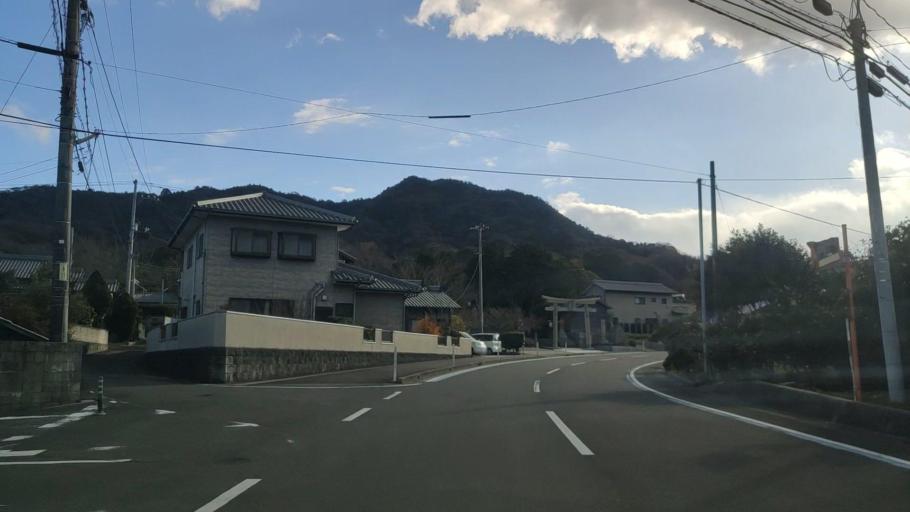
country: JP
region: Hiroshima
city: Innoshima
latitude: 34.2266
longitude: 133.0737
